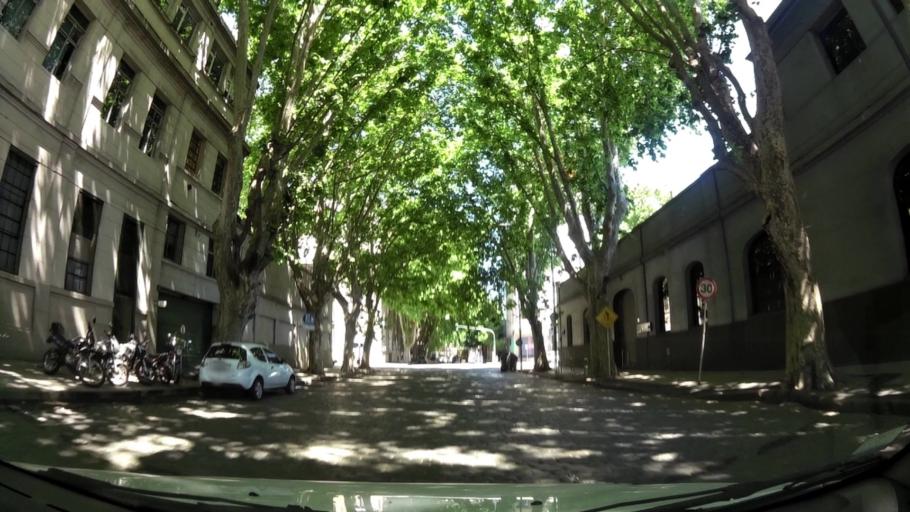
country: AR
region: Buenos Aires F.D.
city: Buenos Aires
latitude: -34.6204
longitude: -58.3664
